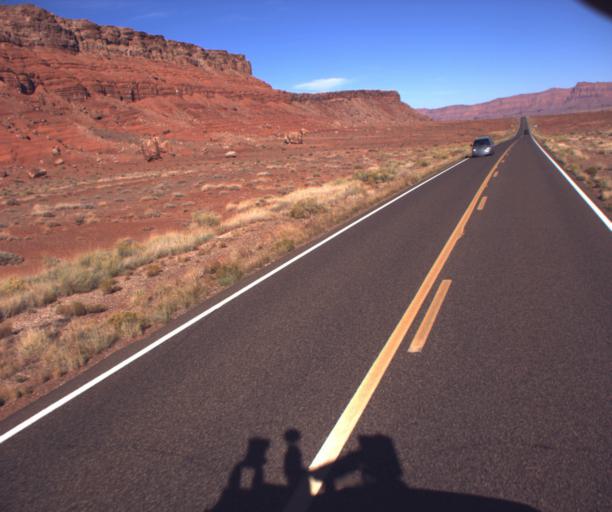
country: US
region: Arizona
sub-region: Coconino County
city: Page
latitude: 36.7477
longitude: -111.7402
